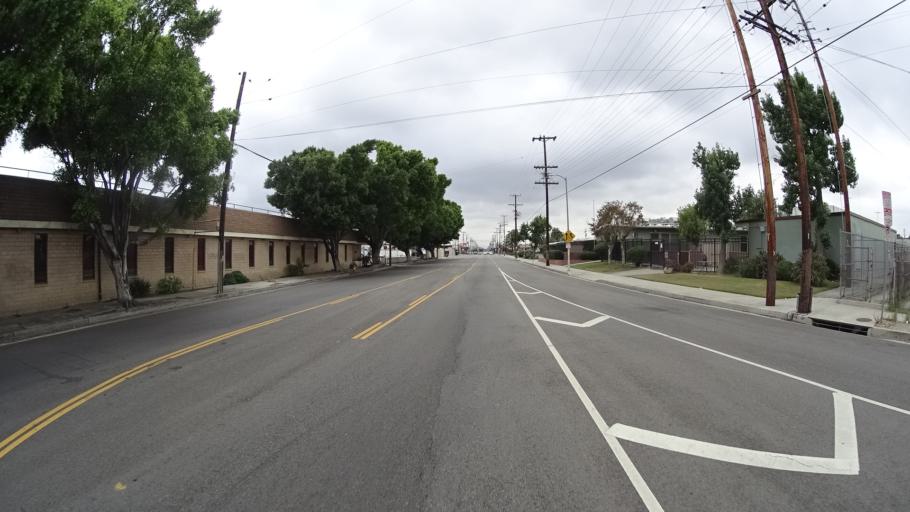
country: US
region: California
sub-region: Los Angeles County
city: Van Nuys
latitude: 34.2061
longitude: -118.4117
